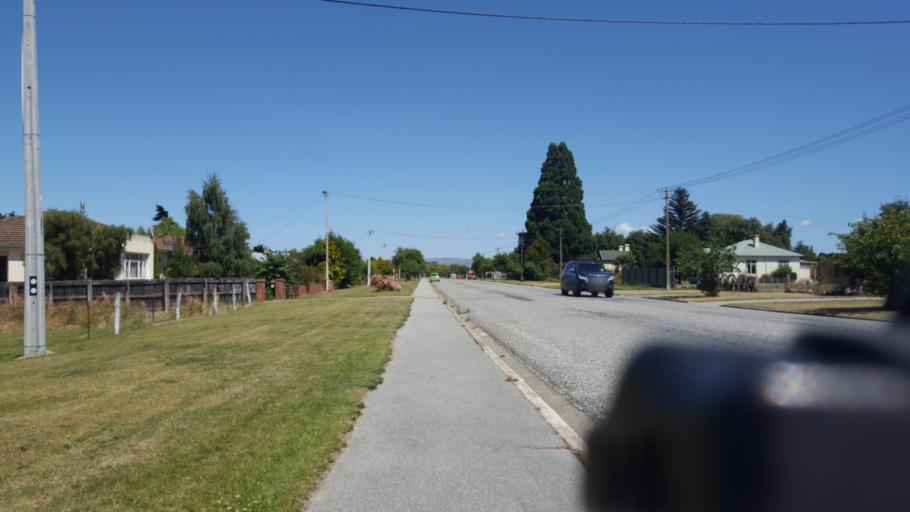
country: NZ
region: Otago
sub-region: Dunedin City
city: Dunedin
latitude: -45.1269
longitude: 170.1047
